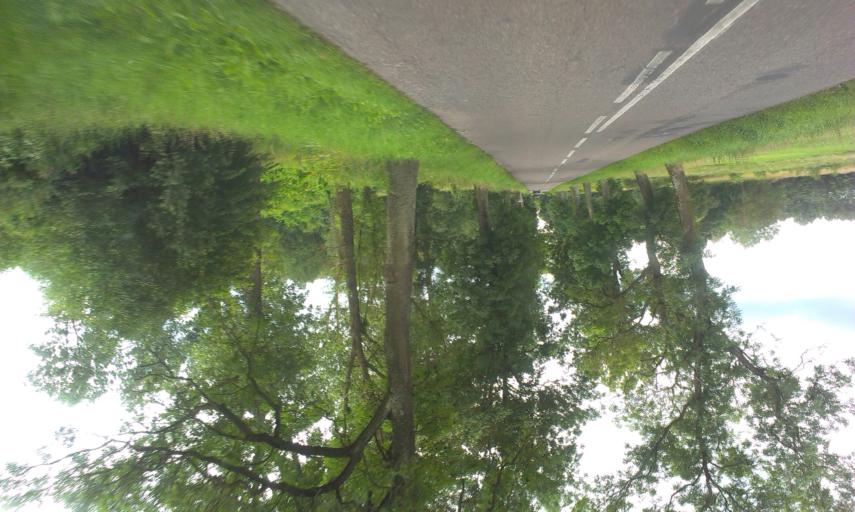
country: PL
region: West Pomeranian Voivodeship
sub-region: Powiat bialogardzki
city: Tychowo
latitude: 53.9204
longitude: 16.2420
